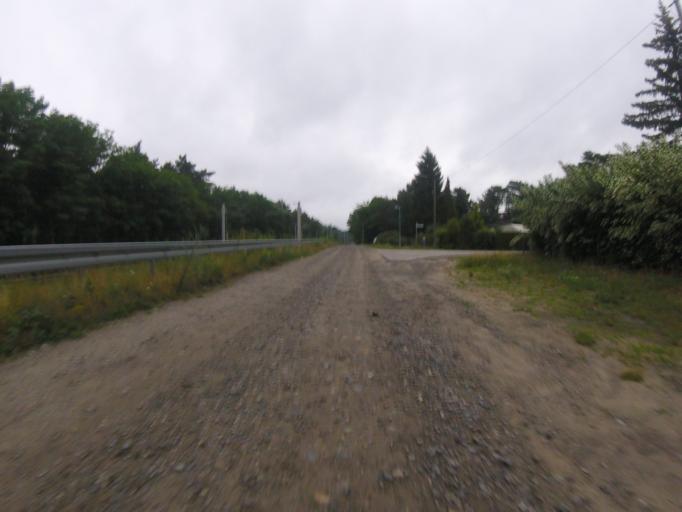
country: DE
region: Brandenburg
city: Bestensee
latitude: 52.2199
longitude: 13.6210
